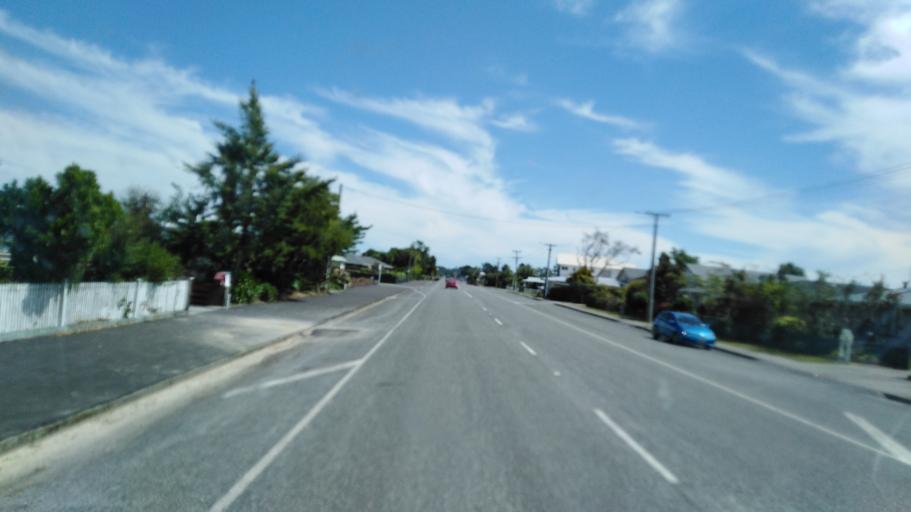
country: NZ
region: West Coast
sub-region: Buller District
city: Westport
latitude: -41.7541
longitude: 171.6092
